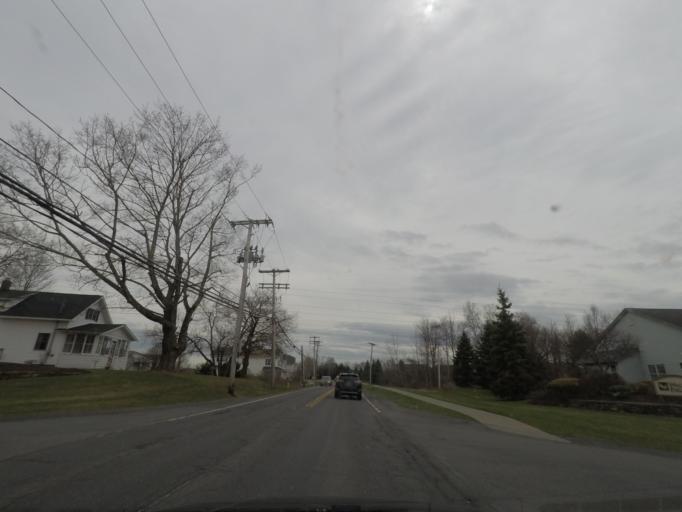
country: US
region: New York
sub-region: Albany County
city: Delmar
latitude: 42.6051
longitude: -73.8184
